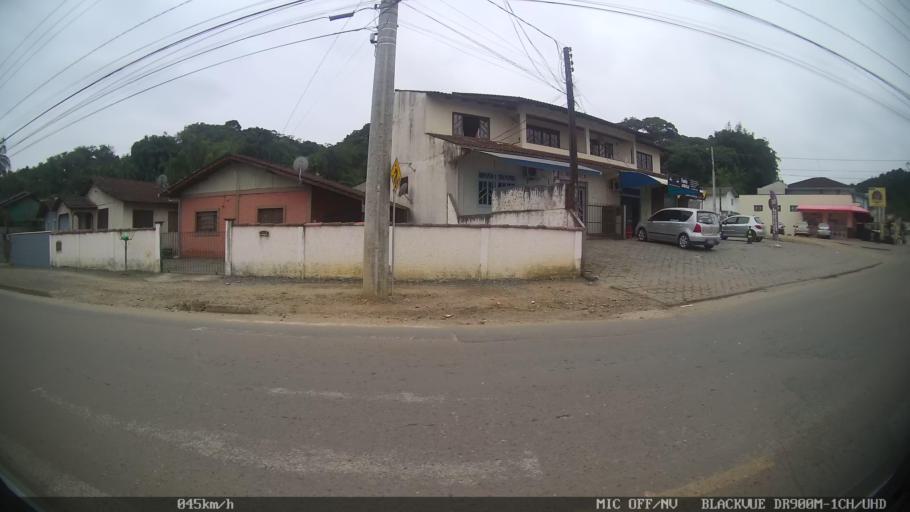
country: BR
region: Santa Catarina
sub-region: Joinville
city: Joinville
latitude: -26.3628
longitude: -48.8238
